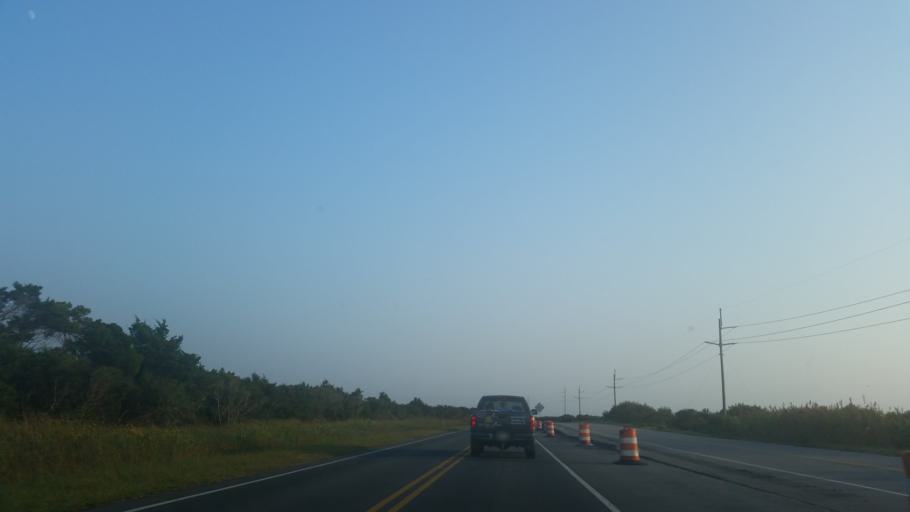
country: US
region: North Carolina
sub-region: Dare County
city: Wanchese
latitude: 35.6627
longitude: -75.4789
